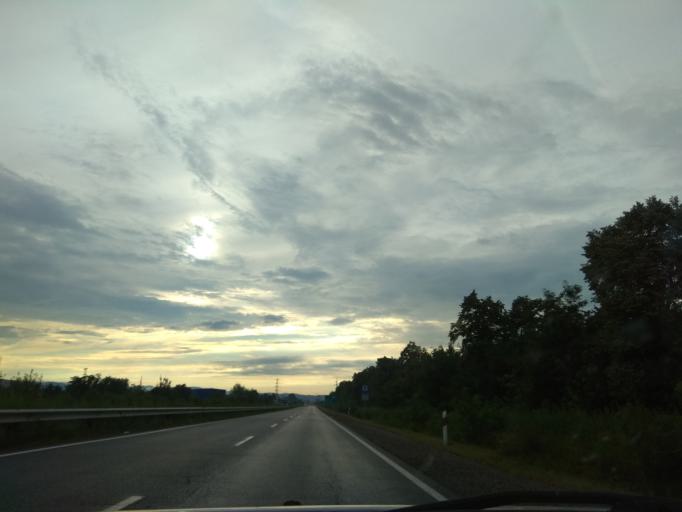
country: HU
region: Borsod-Abauj-Zemplen
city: Felsozsolca
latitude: 48.1134
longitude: 20.8667
